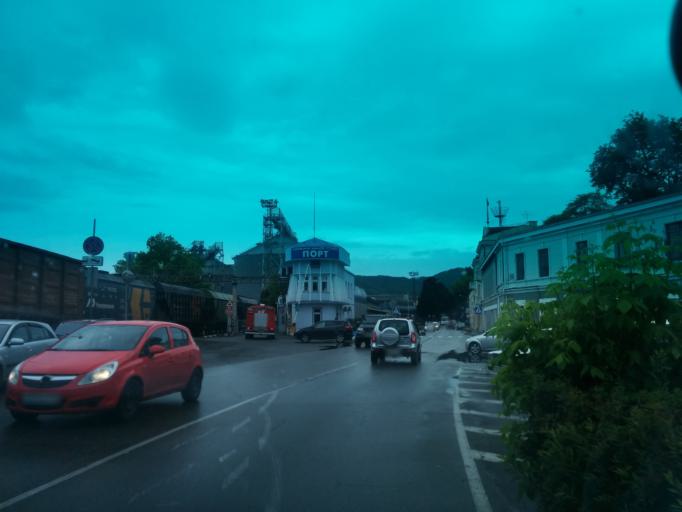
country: RU
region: Krasnodarskiy
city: Tuapse
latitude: 44.0952
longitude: 39.0700
